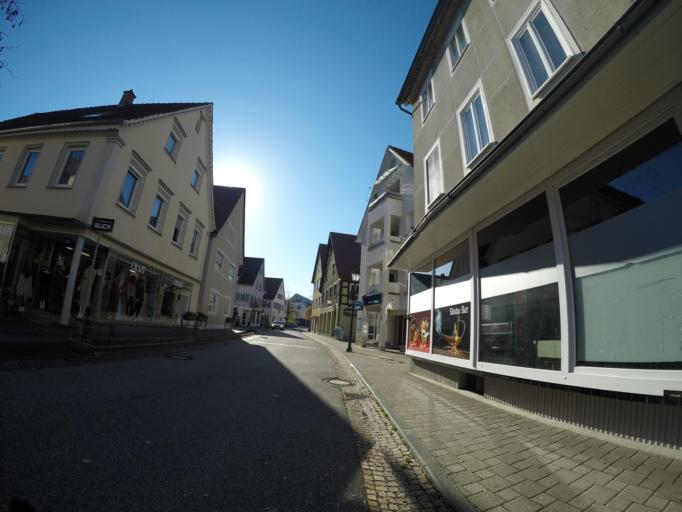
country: DE
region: Baden-Wuerttemberg
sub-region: Tuebingen Region
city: Saulgau
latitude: 48.0167
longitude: 9.4992
